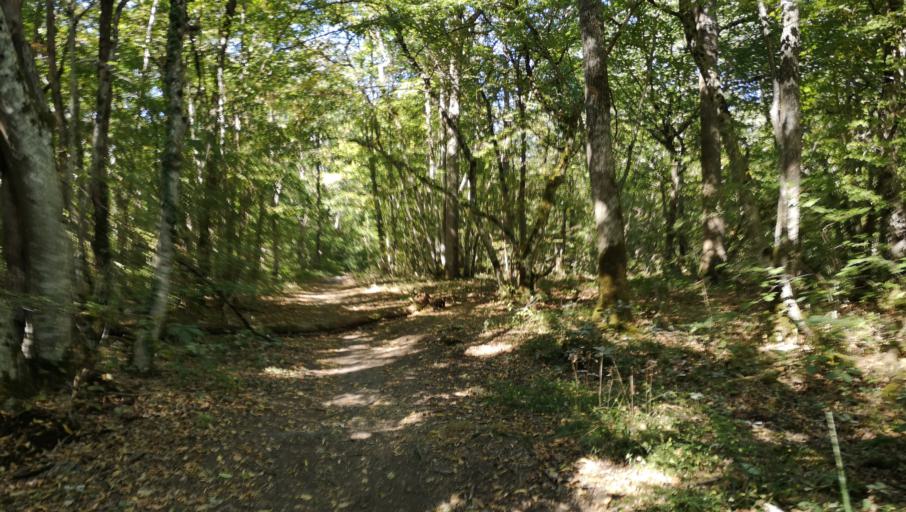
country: FR
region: Centre
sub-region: Departement du Loiret
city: Saran
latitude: 47.9613
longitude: 1.9017
